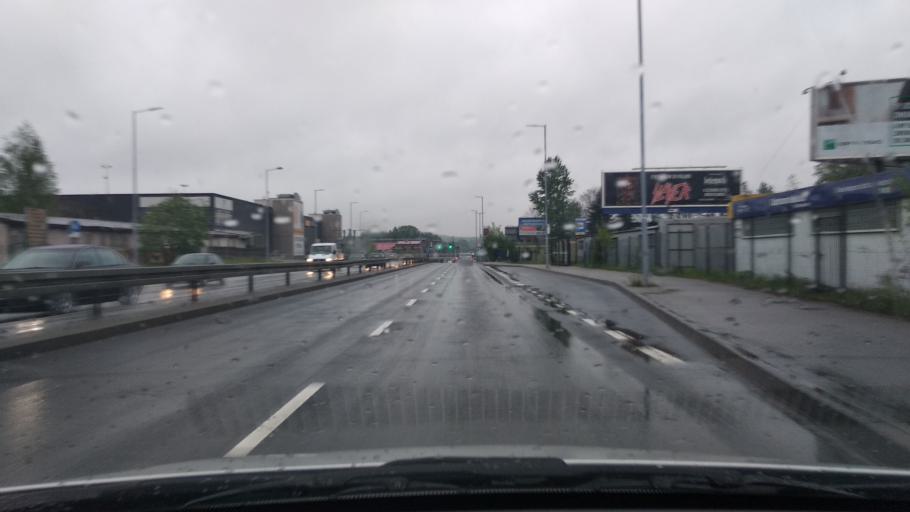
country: PL
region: Silesian Voivodeship
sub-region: Katowice
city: Katowice
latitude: 50.2614
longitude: 18.9865
